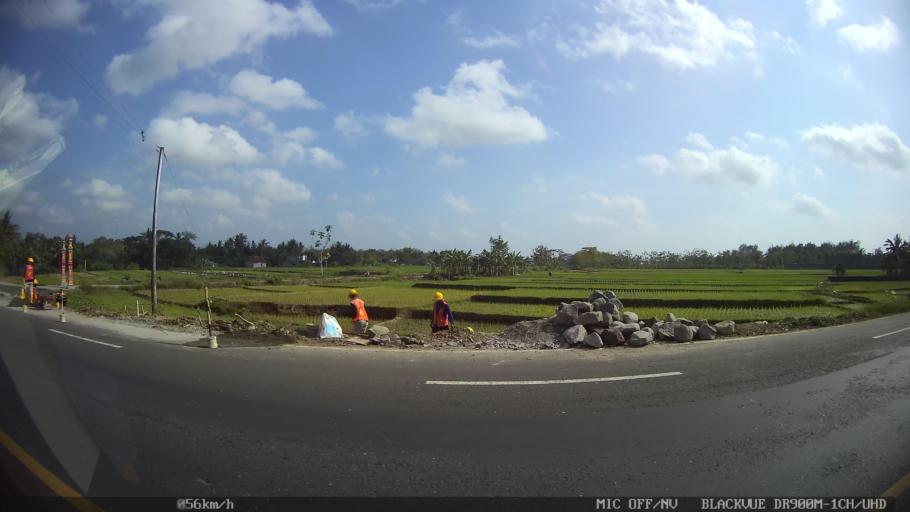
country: ID
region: Daerah Istimewa Yogyakarta
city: Godean
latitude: -7.8147
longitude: 110.2551
